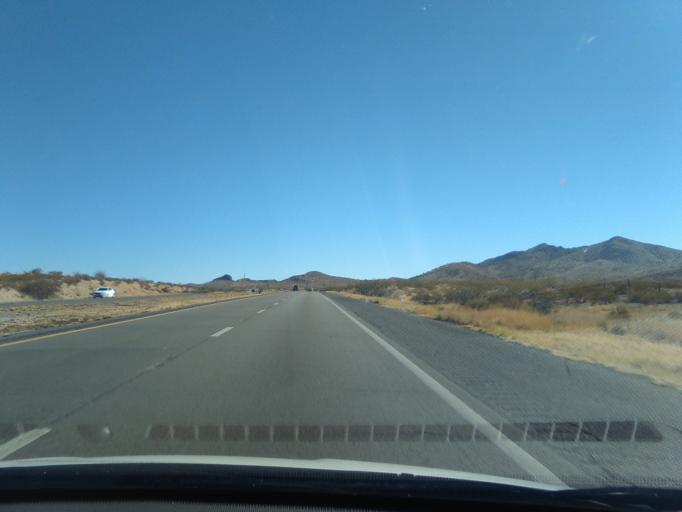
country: US
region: New Mexico
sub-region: Hidalgo County
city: Lordsburg
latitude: 32.2242
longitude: -109.0380
